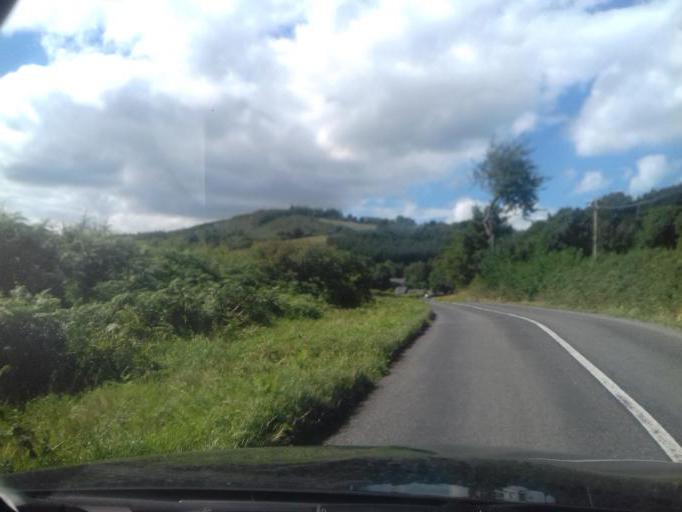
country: IE
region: Munster
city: Carrick-on-Suir
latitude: 52.4012
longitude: -7.4795
